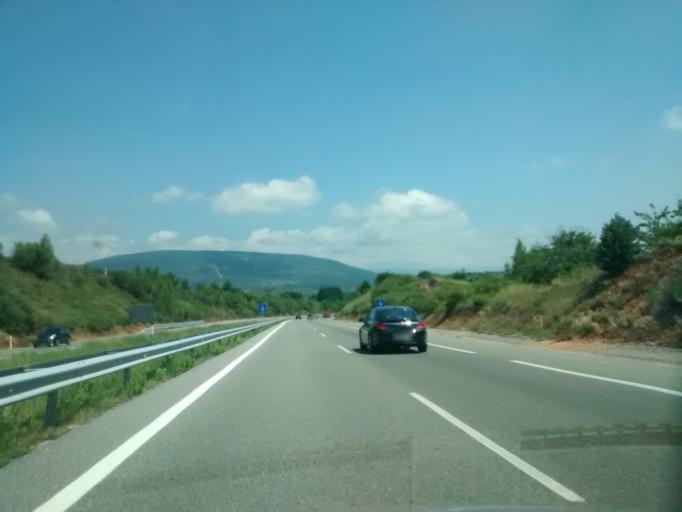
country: ES
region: Castille and Leon
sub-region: Provincia de Leon
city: Congosto
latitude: 42.5862
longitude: -6.5264
